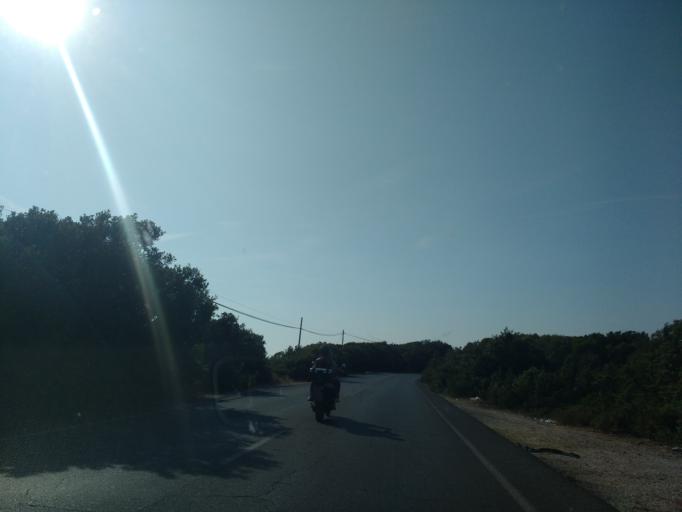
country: IT
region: Latium
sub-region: Citta metropolitana di Roma Capitale
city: Acilia-Castel Fusano-Ostia Antica
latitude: 41.6906
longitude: 12.3685
